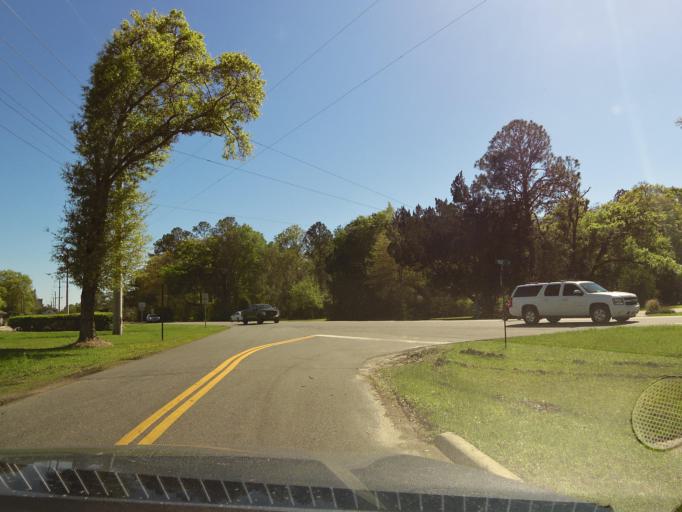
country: US
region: Florida
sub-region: Bradford County
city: Starke
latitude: 29.9304
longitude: -82.1023
